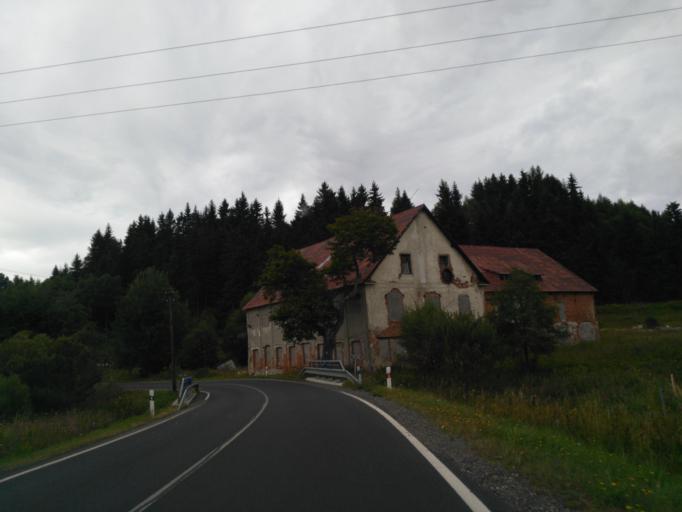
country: CZ
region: Karlovarsky
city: Abertamy
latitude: 50.3692
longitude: 12.8293
